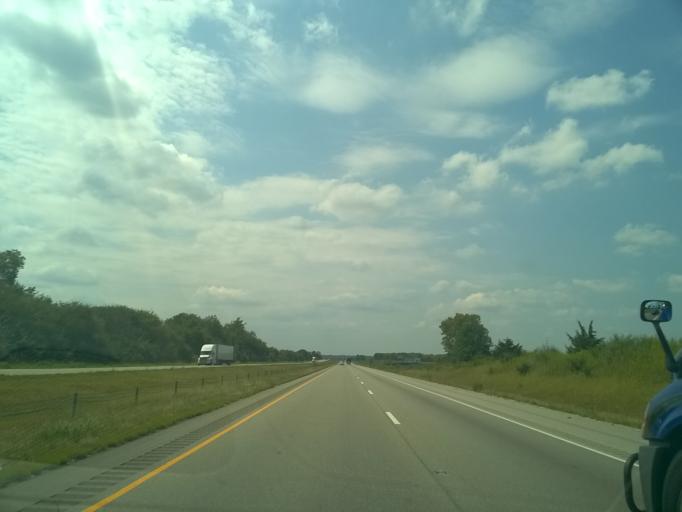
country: US
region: Indiana
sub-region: Morgan County
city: Monrovia
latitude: 39.5739
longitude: -86.6196
